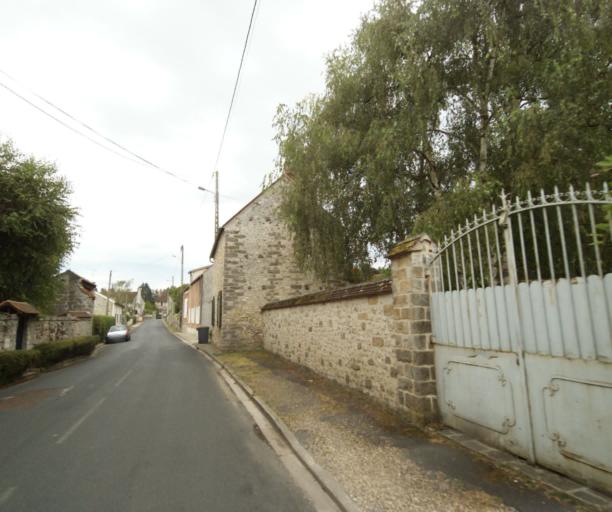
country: FR
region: Ile-de-France
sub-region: Departement de Seine-et-Marne
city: Cely
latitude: 48.4606
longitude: 2.5258
